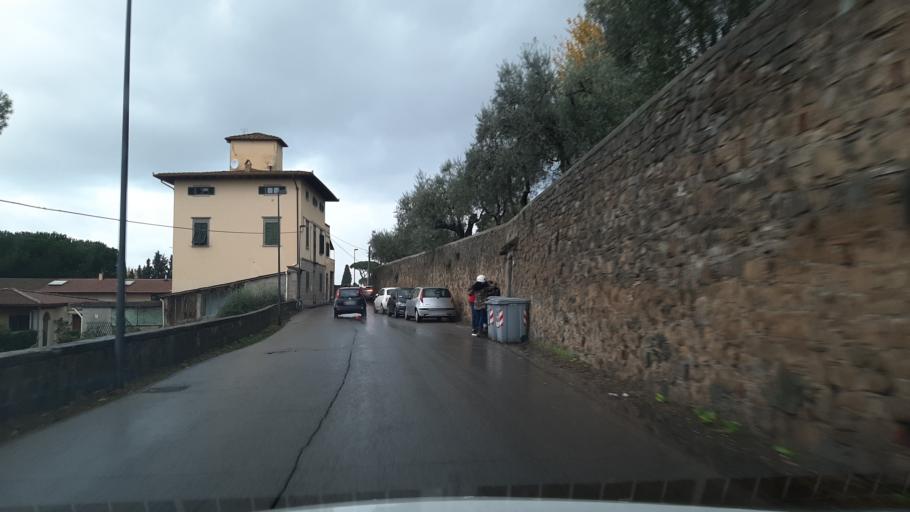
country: IT
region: Tuscany
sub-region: Province of Florence
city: Florence
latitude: 43.8097
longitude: 11.2586
